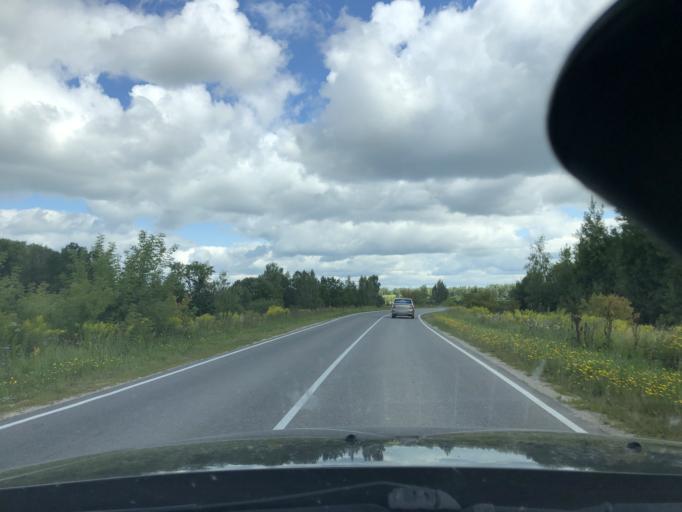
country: RU
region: Tula
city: Yasnogorsk
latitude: 54.4475
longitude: 37.7066
